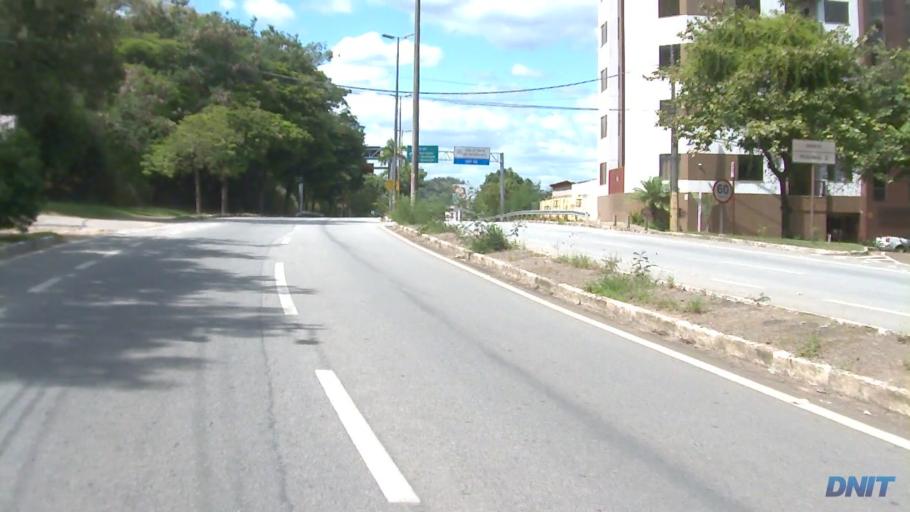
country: BR
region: Minas Gerais
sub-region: Coronel Fabriciano
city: Coronel Fabriciano
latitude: -19.5084
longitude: -42.5790
